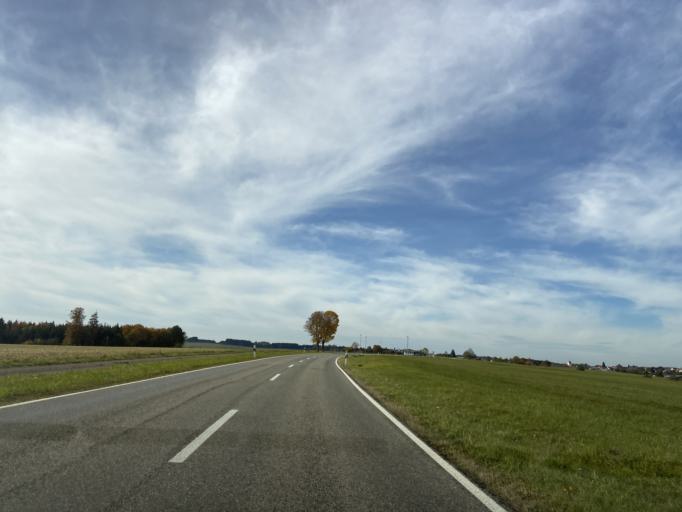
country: DE
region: Baden-Wuerttemberg
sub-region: Tuebingen Region
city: Leibertingen
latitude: 48.0538
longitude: 9.0713
